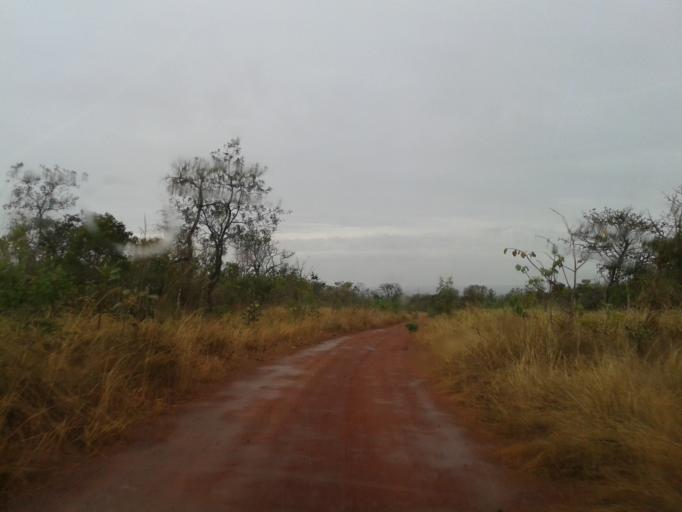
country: BR
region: Minas Gerais
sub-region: Campina Verde
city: Campina Verde
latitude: -19.3262
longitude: -49.5153
